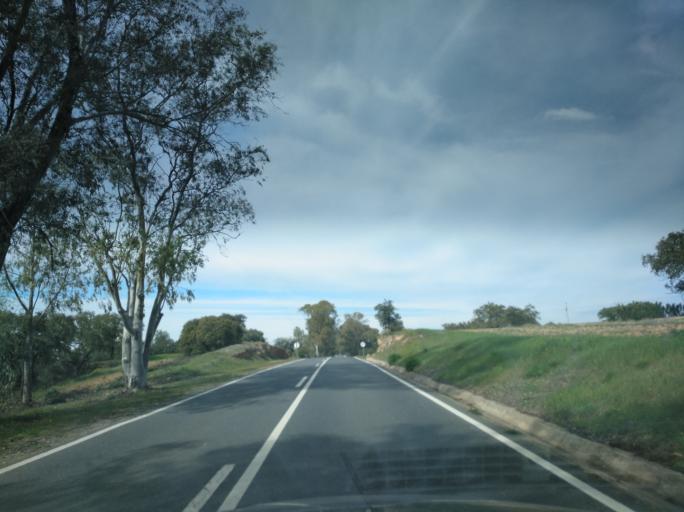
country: PT
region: Beja
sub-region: Mertola
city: Mertola
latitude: 37.7232
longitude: -7.7629
